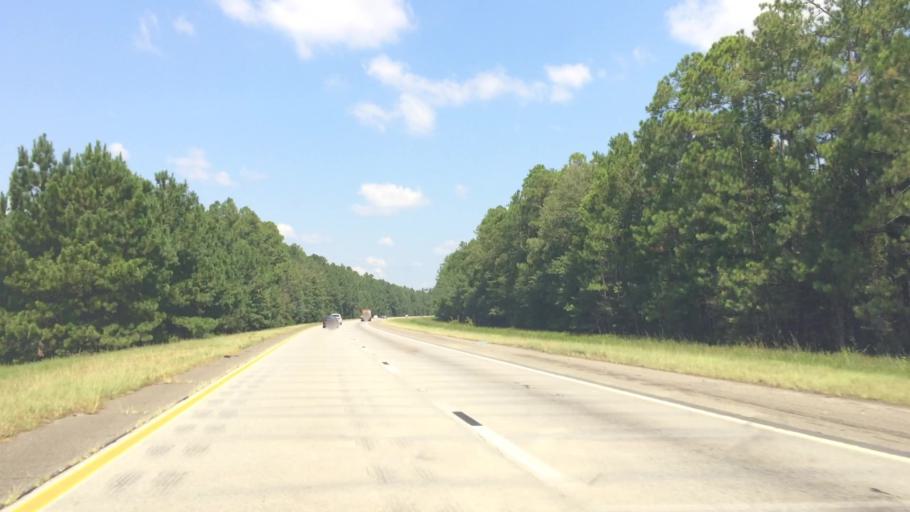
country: US
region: South Carolina
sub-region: Colleton County
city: Walterboro
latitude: 33.0398
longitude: -80.6691
